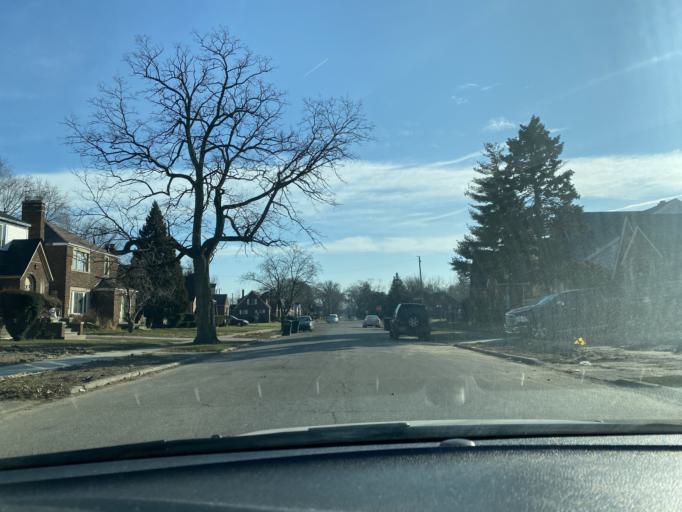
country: US
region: Michigan
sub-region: Wayne County
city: Grosse Pointe Park
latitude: 42.4071
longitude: -82.9467
